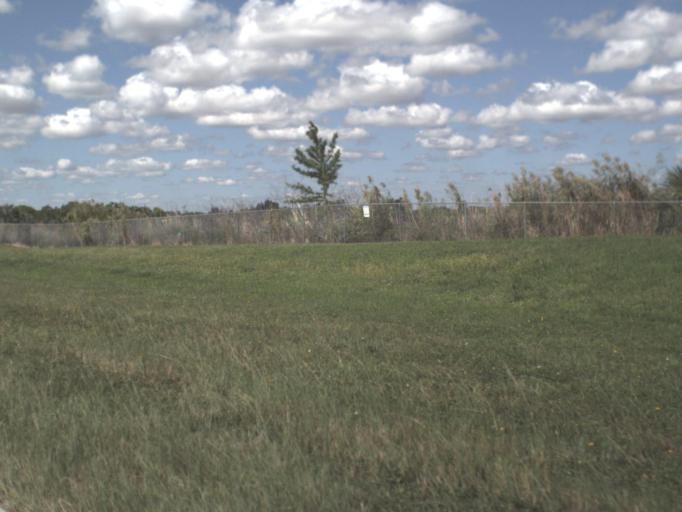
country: US
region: Florida
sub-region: Palm Beach County
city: Boca Pointe
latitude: 26.3053
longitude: -80.1602
